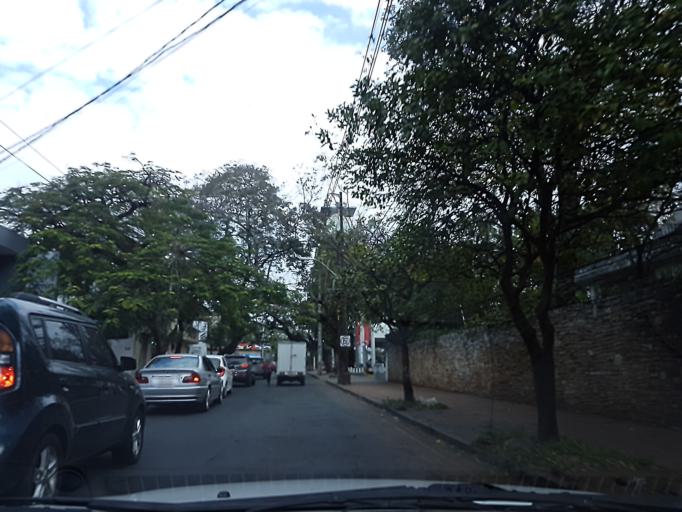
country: PY
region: Central
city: Lambare
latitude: -25.2954
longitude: -57.5745
